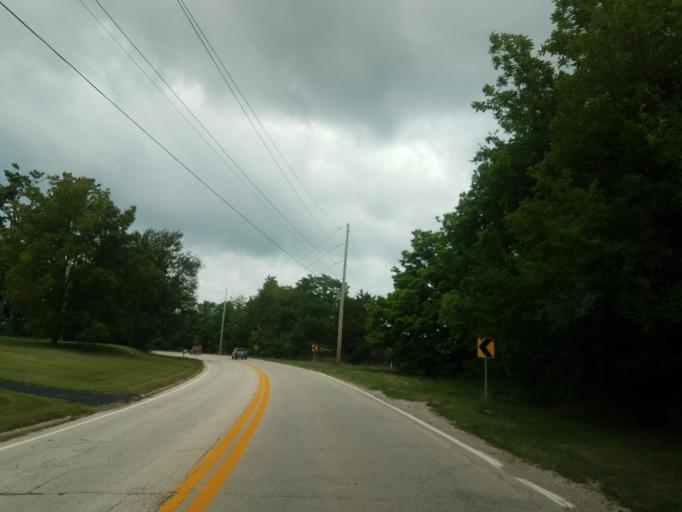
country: US
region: Illinois
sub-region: McLean County
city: Bloomington
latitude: 40.4827
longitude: -89.0309
